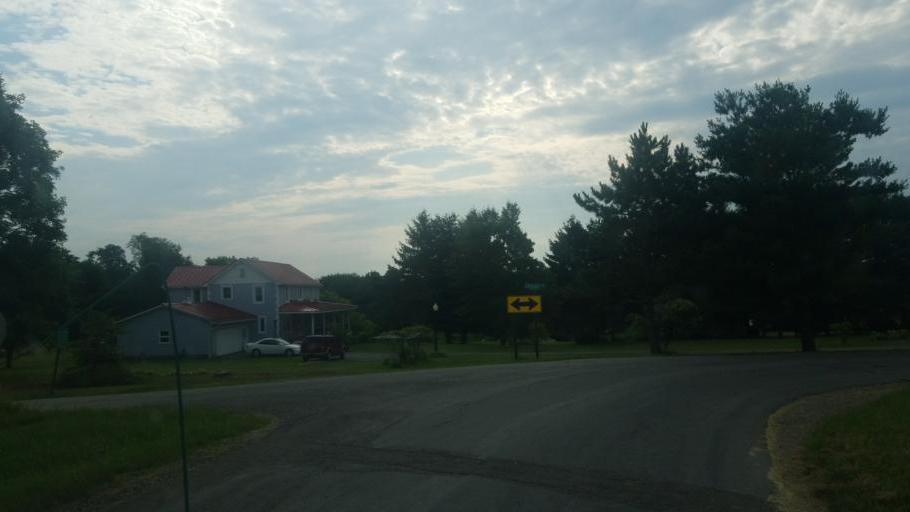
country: US
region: Ohio
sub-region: Wayne County
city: Wooster
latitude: 40.7853
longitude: -81.9947
